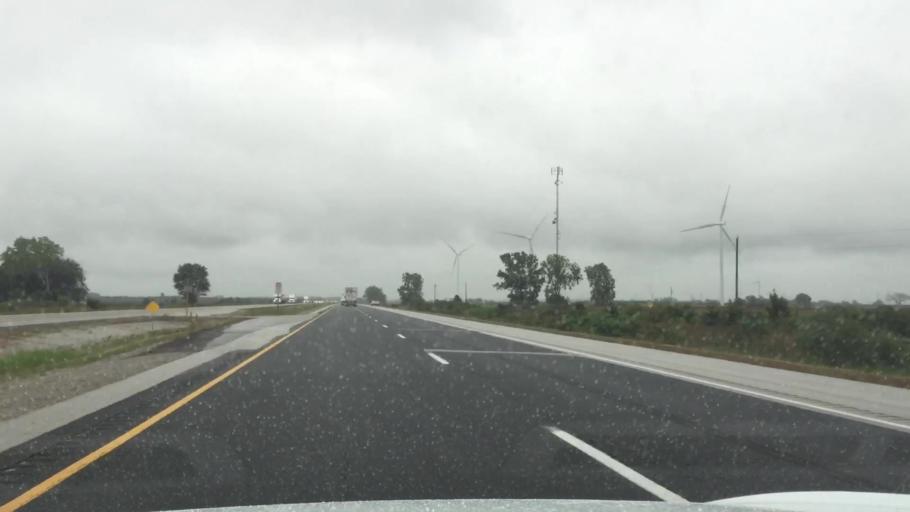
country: CA
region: Ontario
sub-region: Lambton County
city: Walpole Island
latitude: 42.3244
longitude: -82.2468
